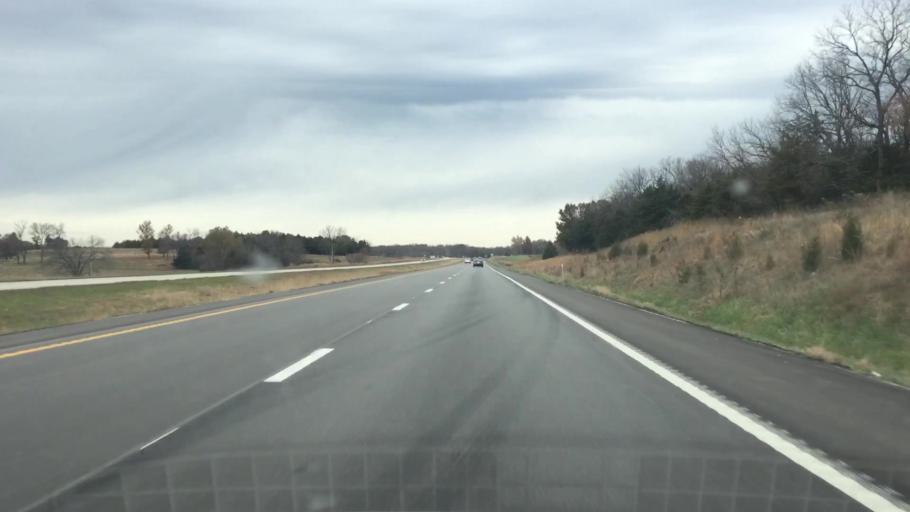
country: US
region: Missouri
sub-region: Saint Clair County
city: Osceola
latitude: 38.0017
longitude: -93.6552
